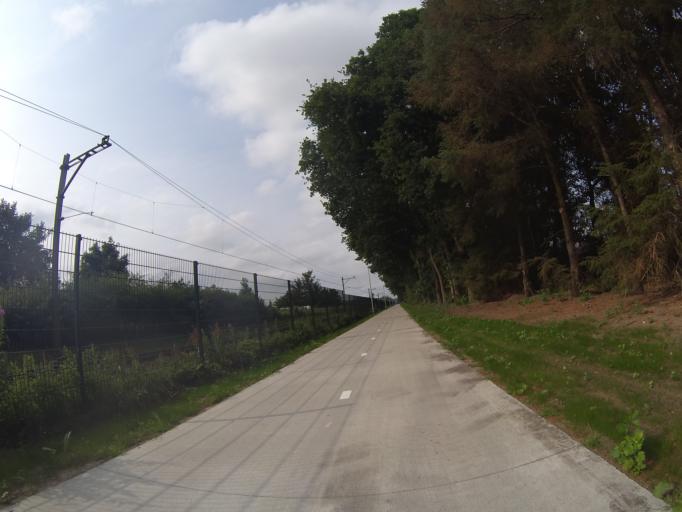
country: NL
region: Drenthe
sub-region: Gemeente Emmen
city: Emmen
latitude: 52.7682
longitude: 6.8981
